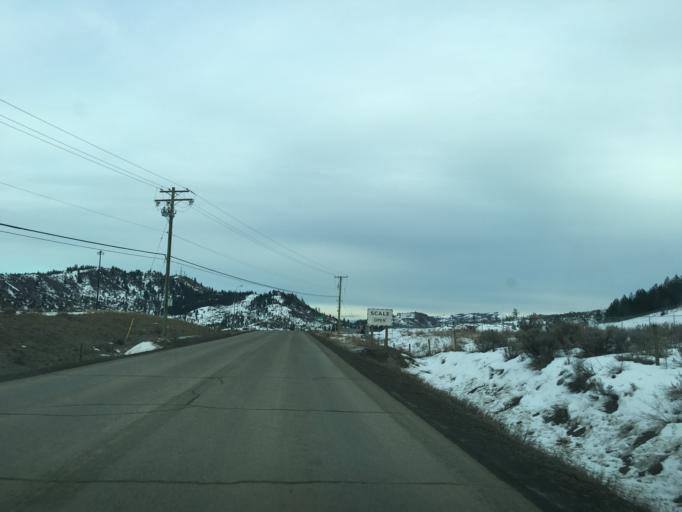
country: CA
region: British Columbia
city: Kamloops
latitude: 50.6649
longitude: -120.4264
